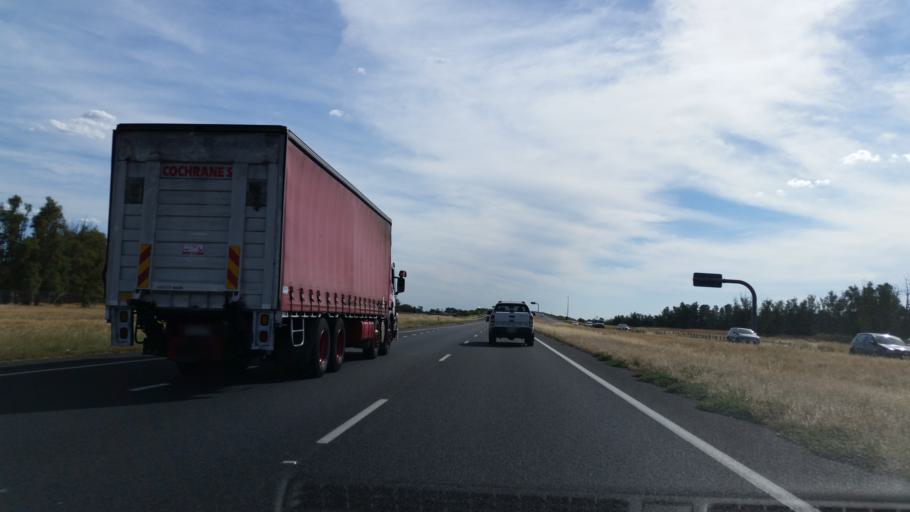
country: AU
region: South Australia
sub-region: Playford
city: Virginia
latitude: -34.6878
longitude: 138.5950
